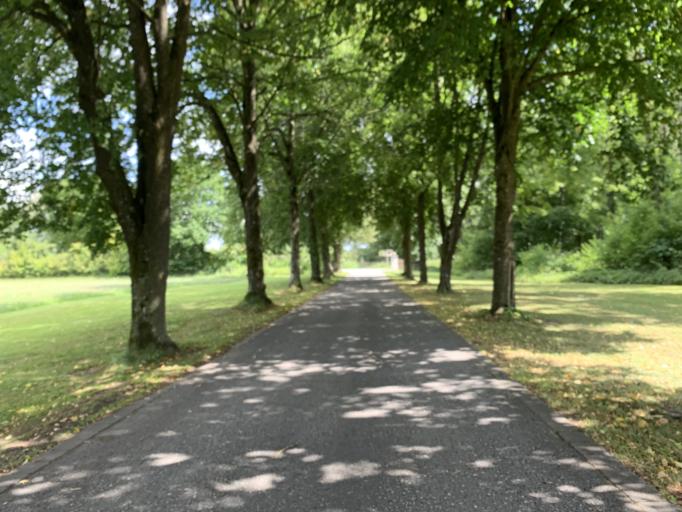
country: DE
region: Bavaria
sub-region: Upper Bavaria
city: Zolling
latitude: 48.4413
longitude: 11.7892
